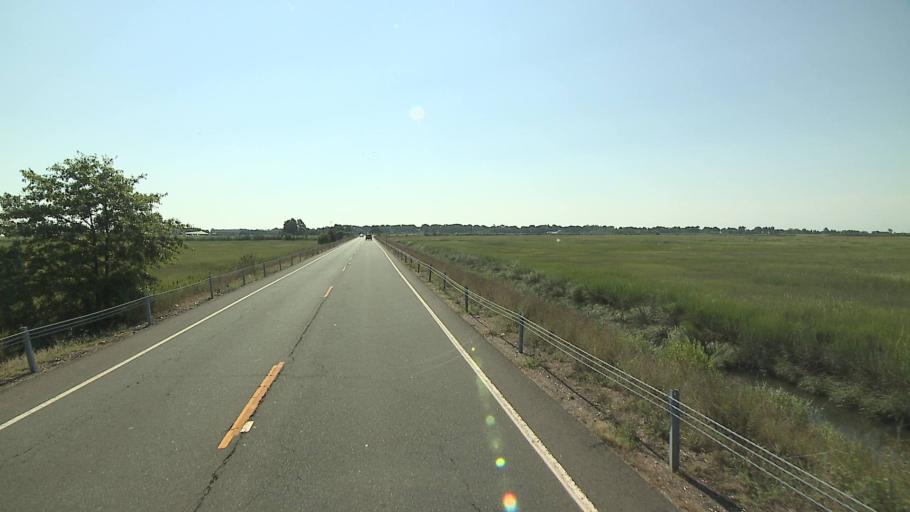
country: US
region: Connecticut
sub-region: Fairfield County
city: Stratford
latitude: 41.1640
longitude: -73.1378
